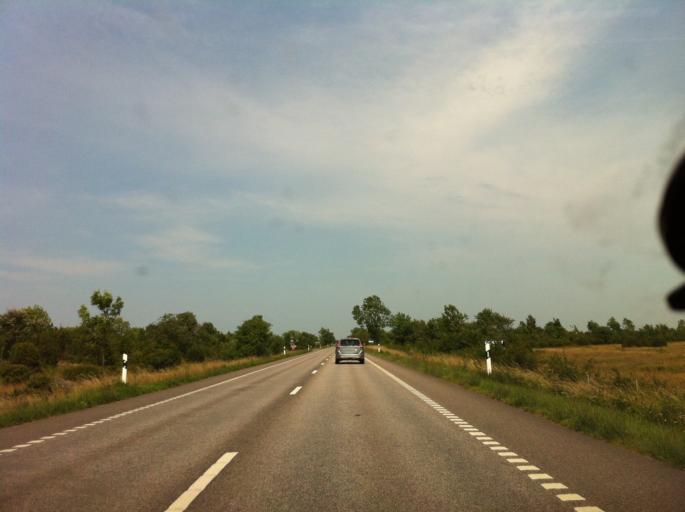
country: SE
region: Kalmar
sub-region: Borgholms Kommun
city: Borgholm
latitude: 56.8117
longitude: 16.5983
